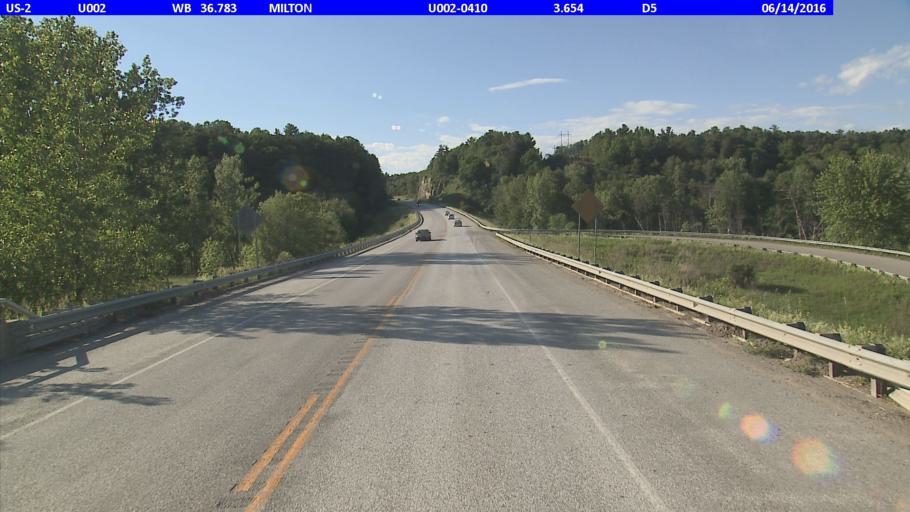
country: US
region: Vermont
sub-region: Chittenden County
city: Colchester
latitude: 44.6040
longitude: -73.2048
